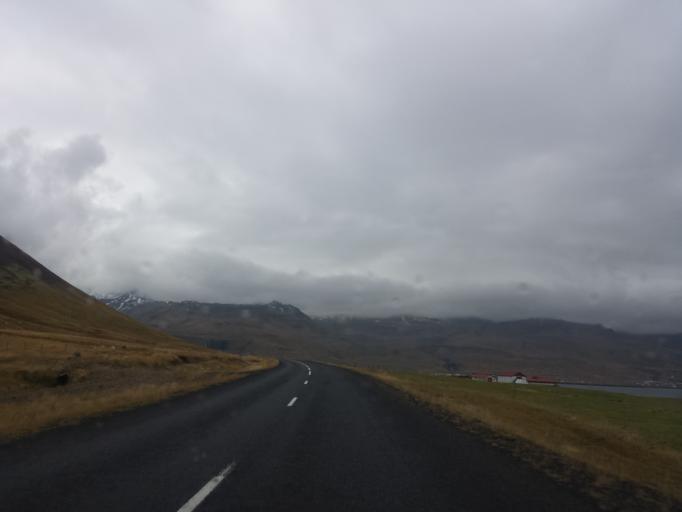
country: IS
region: West
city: Stykkisholmur
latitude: 64.9404
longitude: -23.2004
